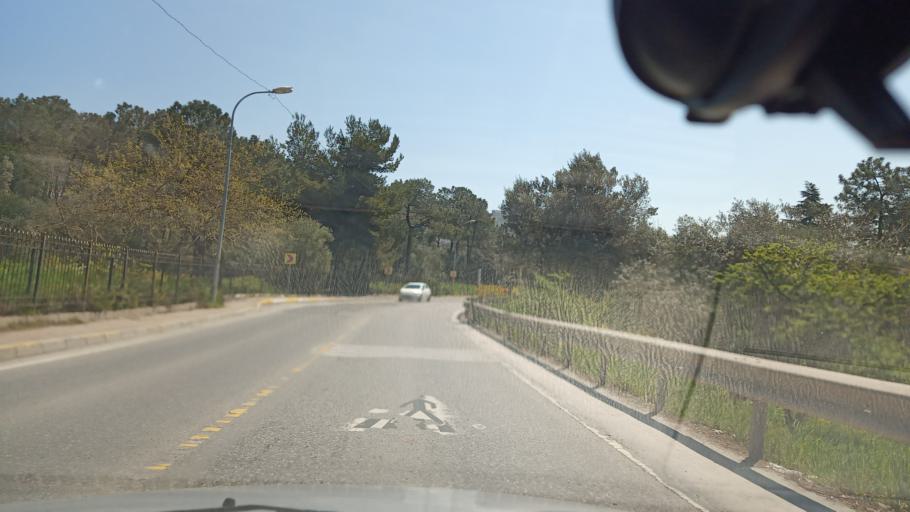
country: TR
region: Istanbul
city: Maltepe
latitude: 40.9478
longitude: 29.1440
